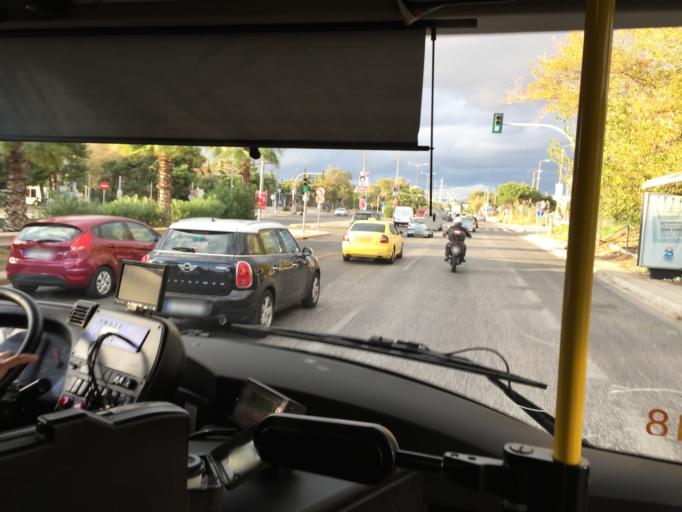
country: GR
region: Attica
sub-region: Nomarchia Athinas
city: Alimos
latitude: 37.8963
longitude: 23.7210
